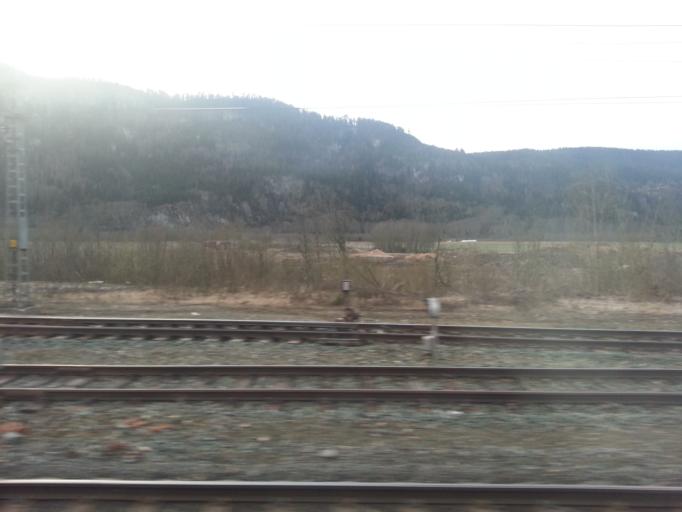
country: NO
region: Sor-Trondelag
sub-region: Midtre Gauldal
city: Storen
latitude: 63.0503
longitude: 10.2846
